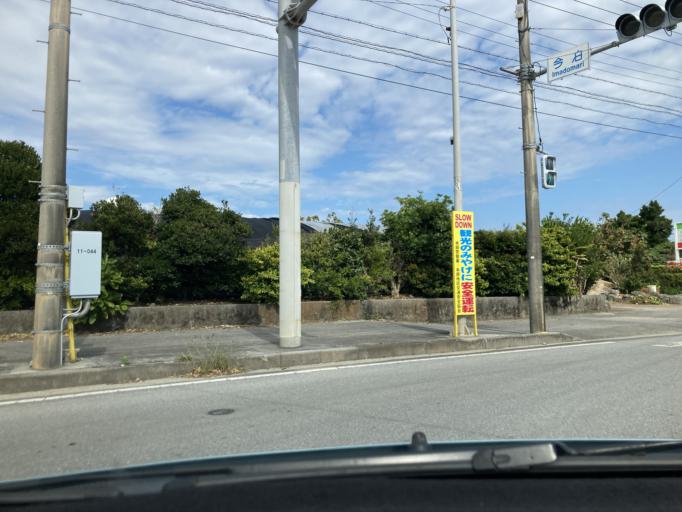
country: JP
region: Okinawa
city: Nago
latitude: 26.7013
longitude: 127.9259
